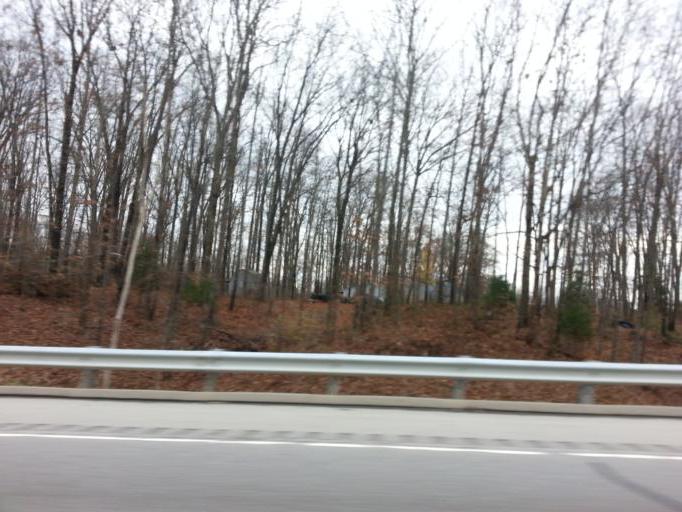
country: US
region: Indiana
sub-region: Ripley County
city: Sunman
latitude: 39.2845
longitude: -85.0732
